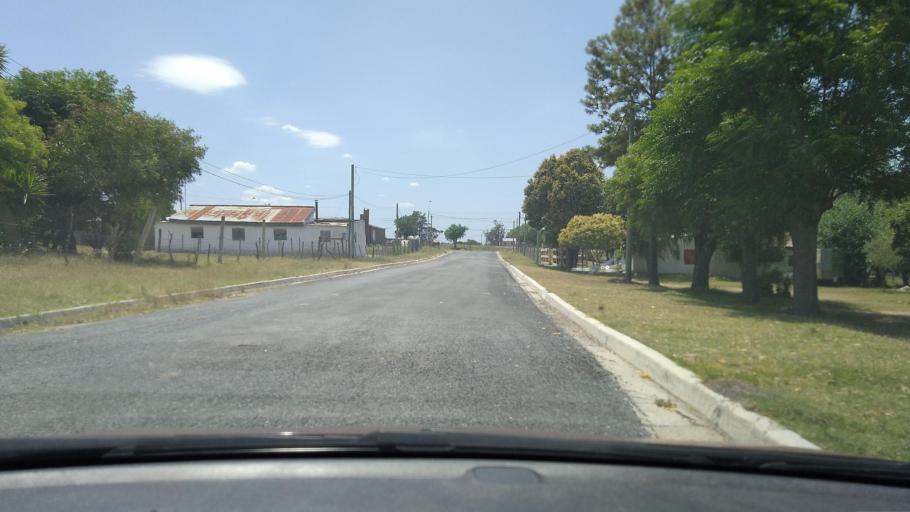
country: UY
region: Canelones
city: Tala
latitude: -34.2015
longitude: -55.7416
